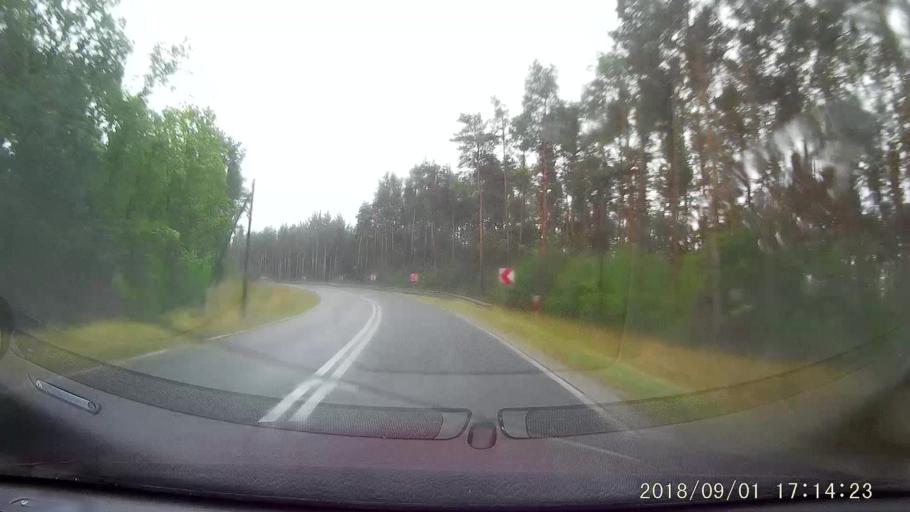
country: PL
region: Lubusz
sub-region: Powiat zielonogorski
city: Nowogrod Bobrzanski
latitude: 51.7843
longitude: 15.2568
